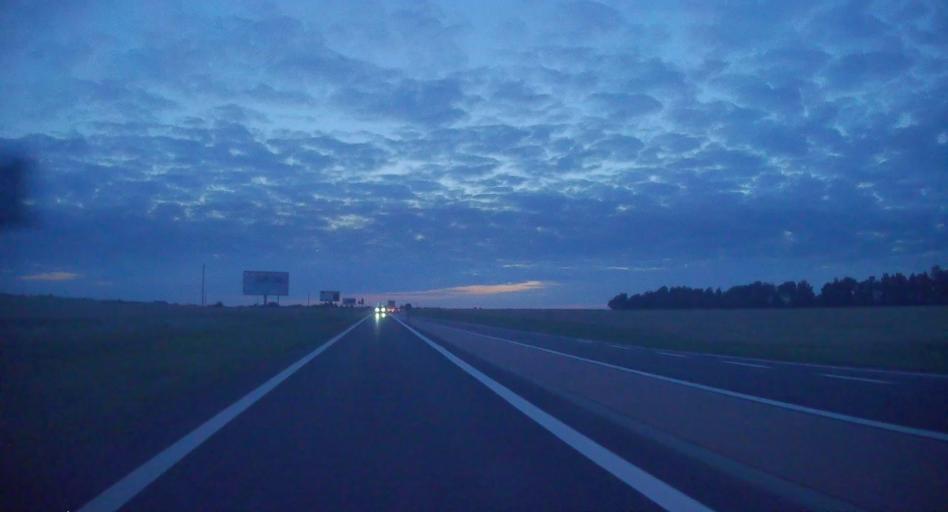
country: PL
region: Silesian Voivodeship
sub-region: Powiat klobucki
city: Klobuck
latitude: 50.8878
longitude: 18.9742
